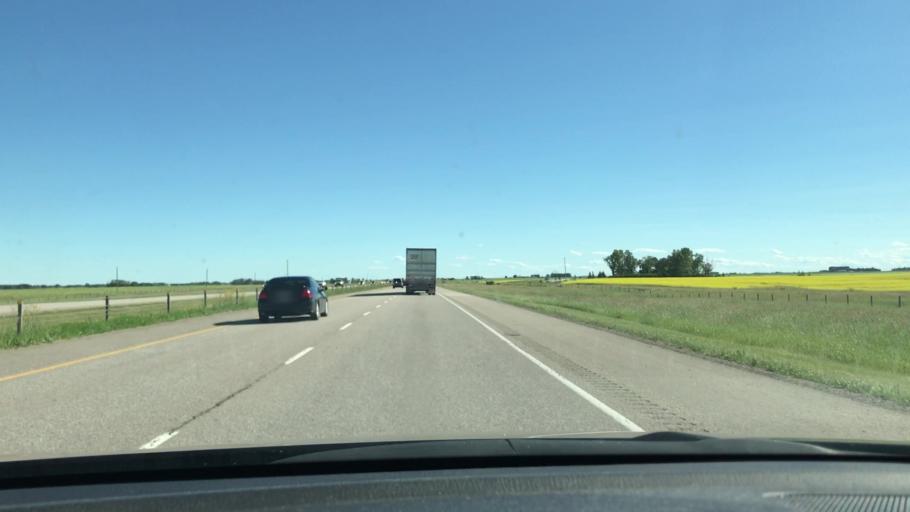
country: CA
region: Alberta
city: Olds
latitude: 51.7162
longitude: -114.0256
